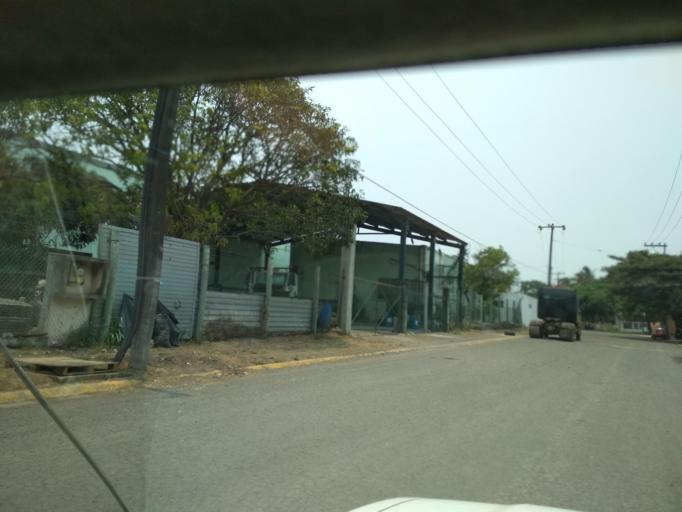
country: MX
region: Veracruz
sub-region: Veracruz
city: Lomas de Rio Medio Cuatro
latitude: 19.1690
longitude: -96.2376
